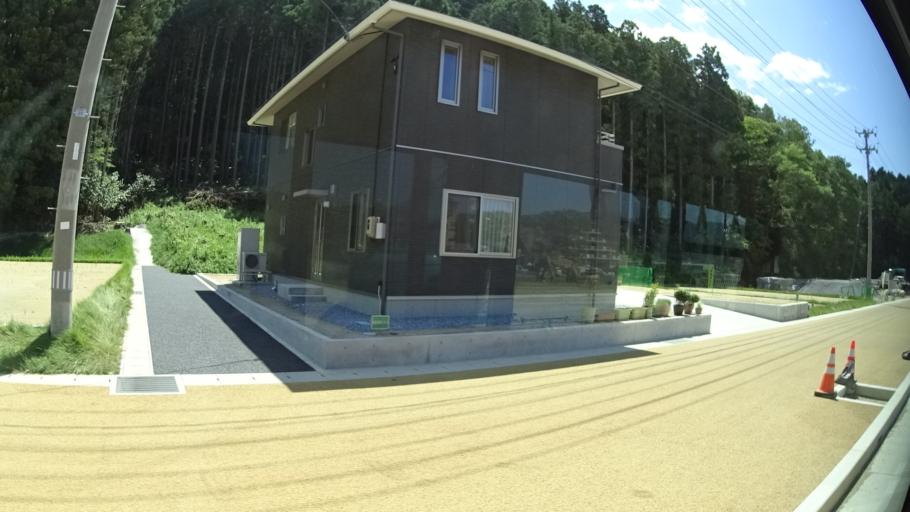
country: JP
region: Iwate
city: Ofunato
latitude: 39.0201
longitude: 141.6355
